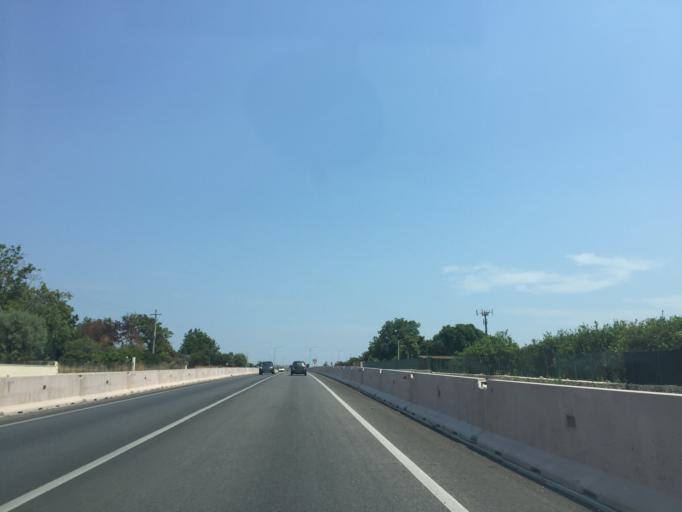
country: IT
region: Sicily
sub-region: Provincia di Siracusa
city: Belvedere
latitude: 37.0725
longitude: 15.2339
